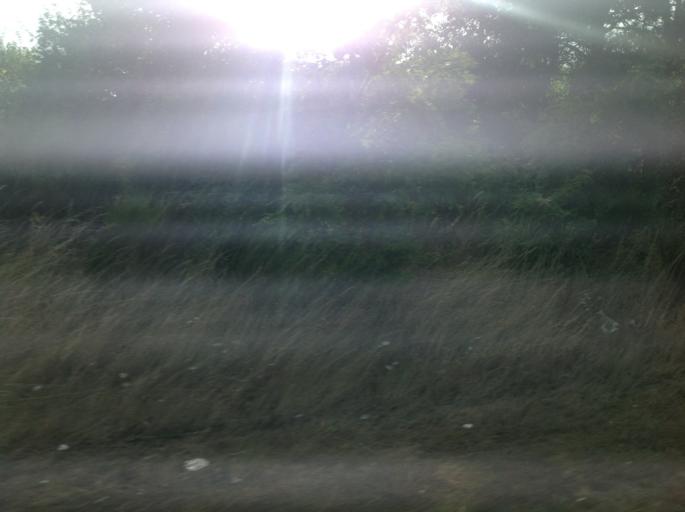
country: GB
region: England
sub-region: Suffolk
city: Felixstowe
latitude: 51.9880
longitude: 1.3199
